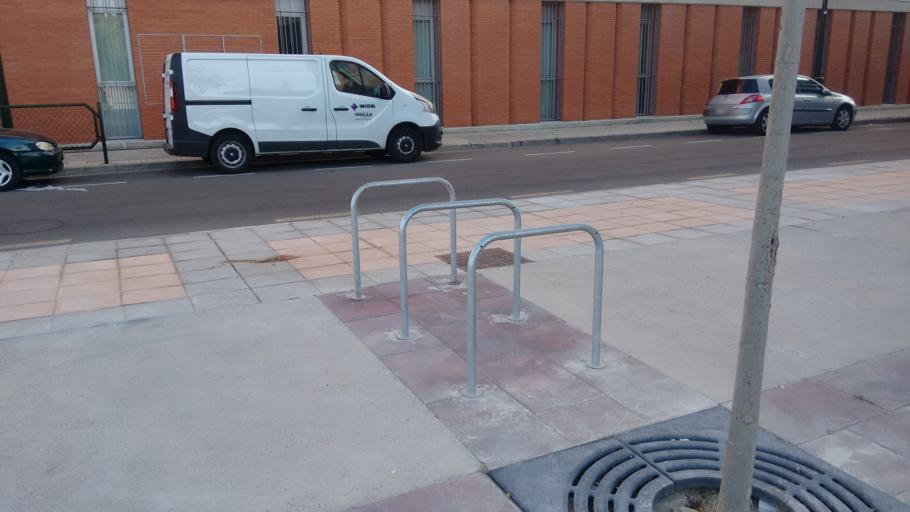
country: ES
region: Aragon
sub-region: Provincia de Zaragoza
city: Zaragoza
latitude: 41.6393
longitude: -0.8630
